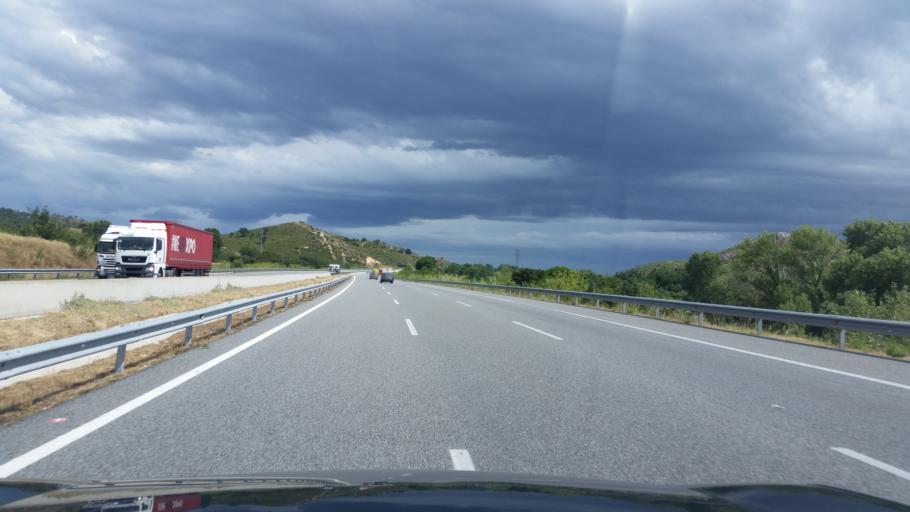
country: ES
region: Catalonia
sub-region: Provincia de Girona
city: Biure
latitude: 42.3523
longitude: 2.9068
